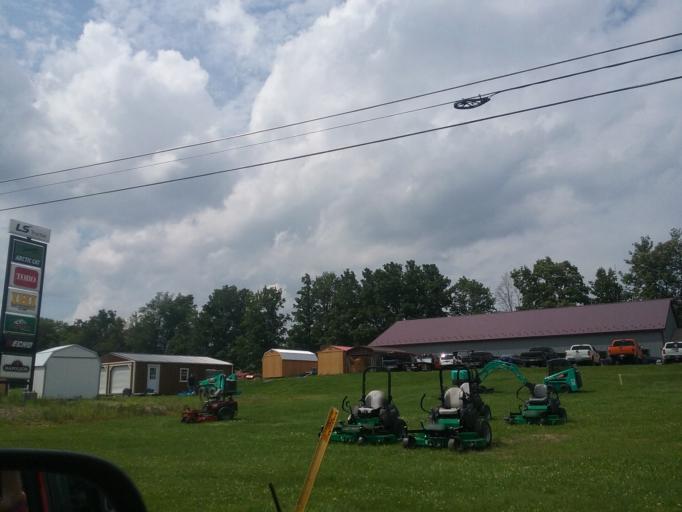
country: US
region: Pennsylvania
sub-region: Tioga County
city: Wellsboro
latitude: 41.7654
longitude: -77.2005
